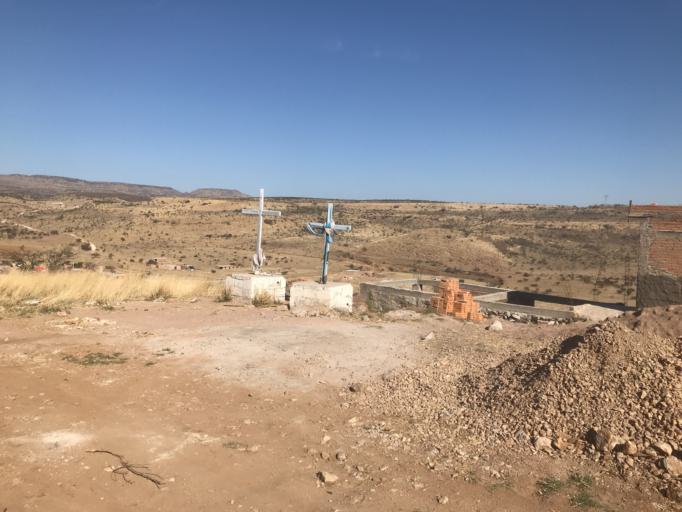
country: MX
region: Durango
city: Victoria de Durango
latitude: 24.0452
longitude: -104.7037
